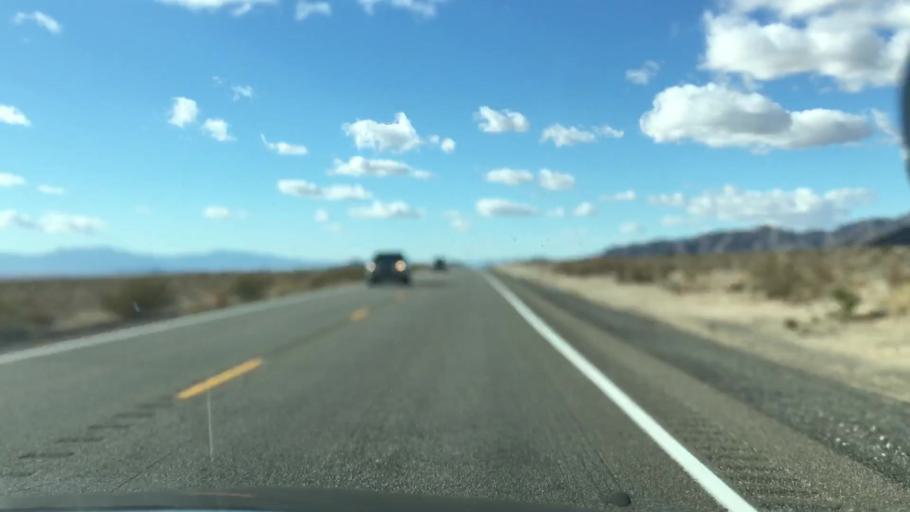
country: US
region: Nevada
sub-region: Nye County
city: Pahrump
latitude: 36.5644
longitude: -116.1167
